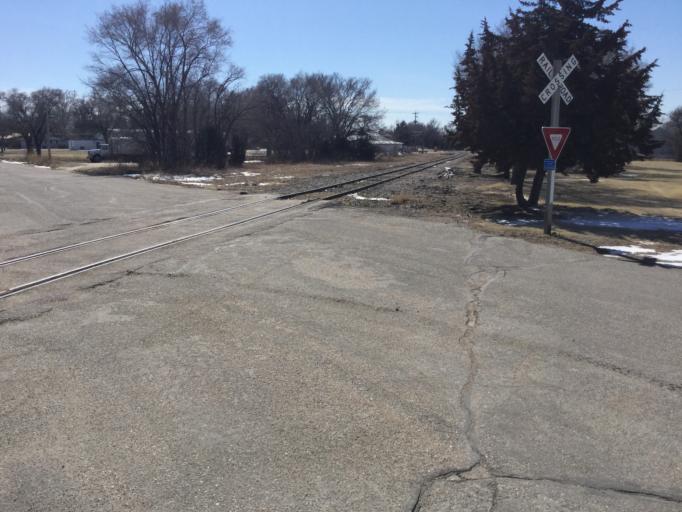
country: US
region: Kansas
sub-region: Sedgwick County
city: Clearwater
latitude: 37.5060
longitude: -97.5086
